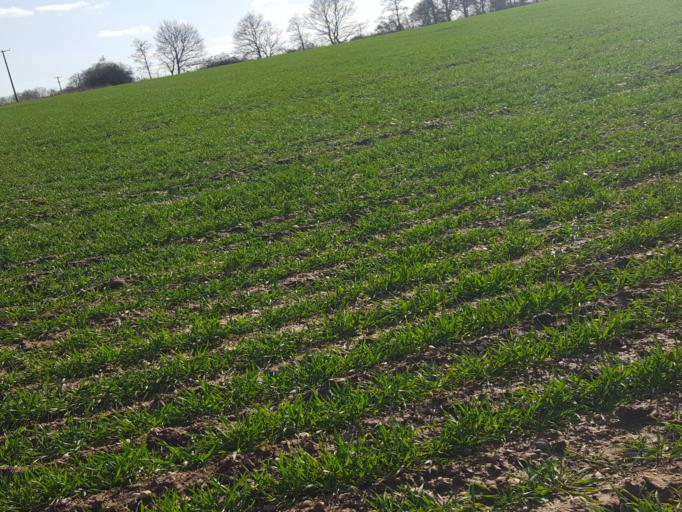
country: GB
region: England
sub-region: Essex
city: Little Clacton
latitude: 51.8671
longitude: 1.1149
